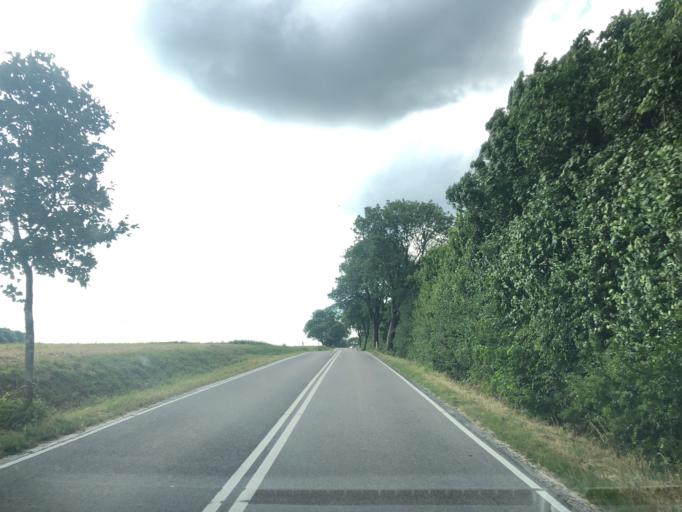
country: DK
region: Zealand
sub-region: Faxe Kommune
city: Haslev
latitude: 55.3077
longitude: 12.0003
